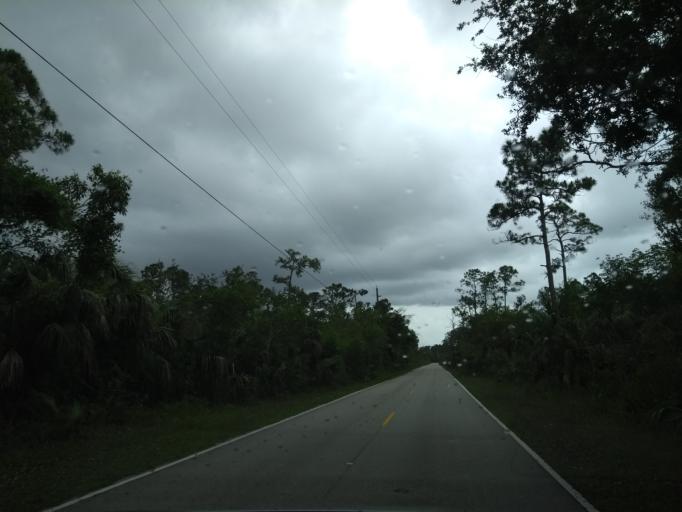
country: US
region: Florida
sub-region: Miami-Dade County
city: The Hammocks
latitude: 25.7500
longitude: -80.9362
